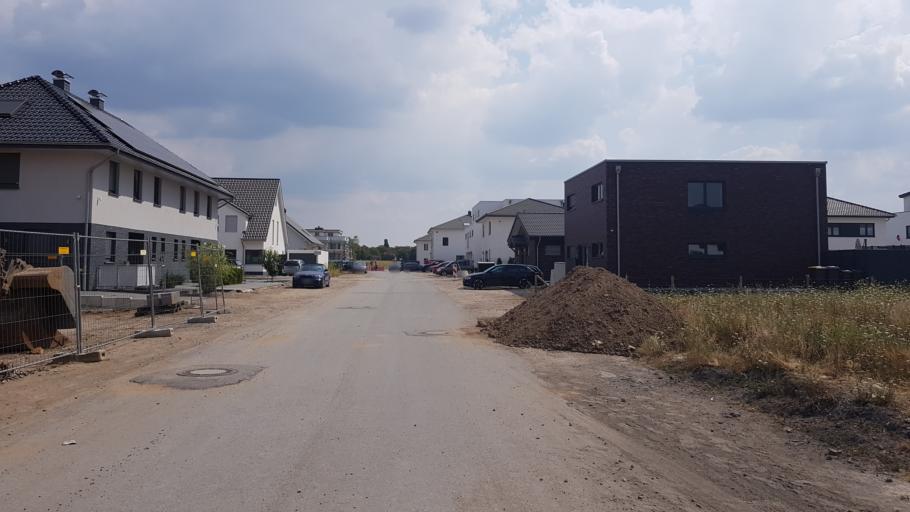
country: DE
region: North Rhine-Westphalia
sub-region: Regierungsbezirk Dusseldorf
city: Kamp-Lintfort
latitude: 51.4444
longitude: 6.5576
